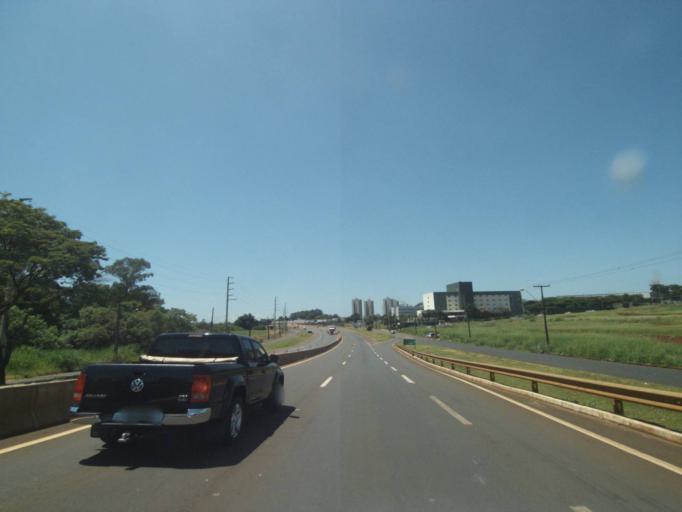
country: BR
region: Parana
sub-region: Londrina
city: Londrina
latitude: -23.3380
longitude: -51.1836
